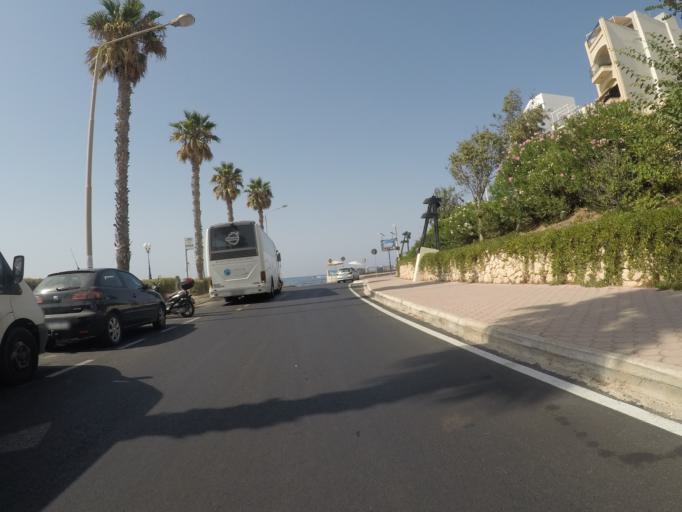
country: MT
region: Saint Paul's Bay
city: San Pawl il-Bahar
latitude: 35.9514
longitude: 14.4087
